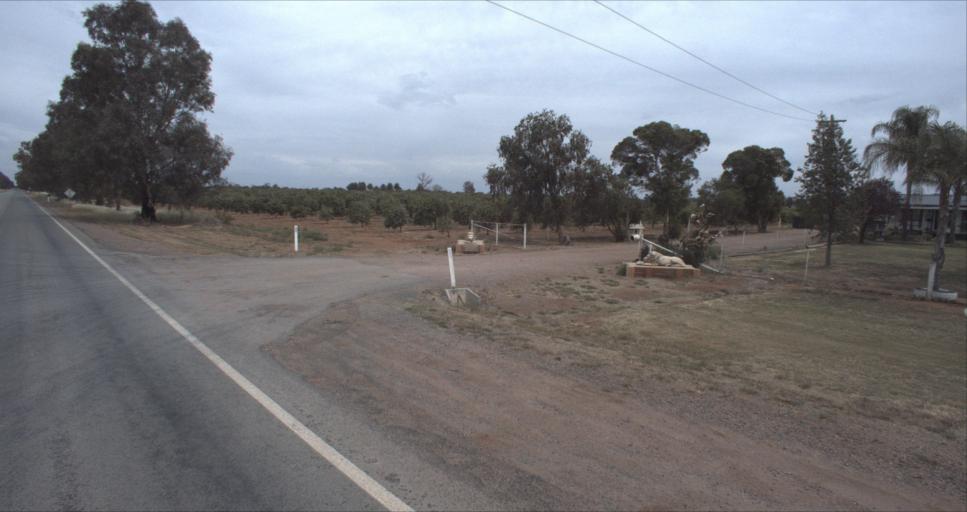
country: AU
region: New South Wales
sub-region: Leeton
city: Leeton
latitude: -34.5051
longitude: 146.4237
